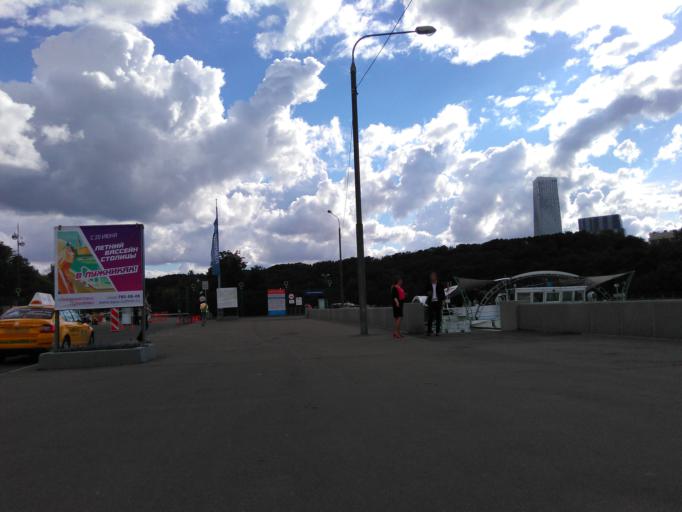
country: RU
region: Moscow
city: Luzhniki
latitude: 55.7264
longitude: 37.5460
